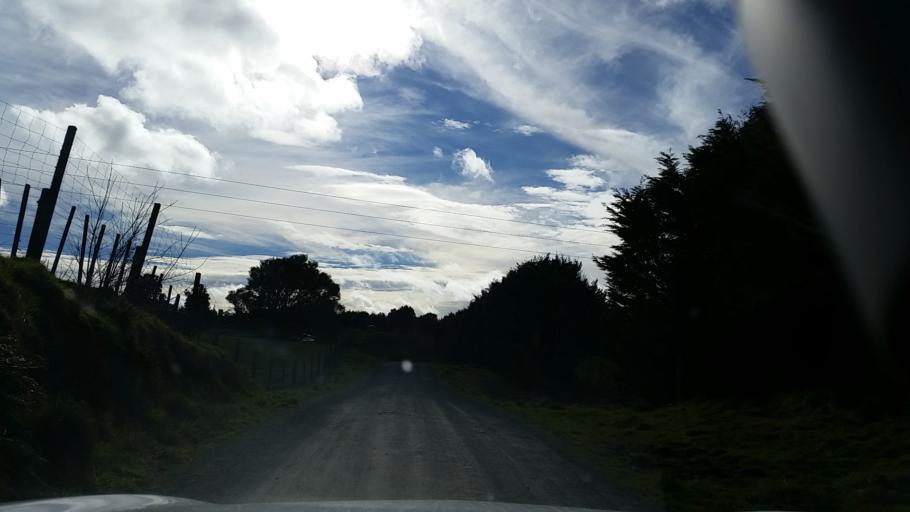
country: NZ
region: Bay of Plenty
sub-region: Rotorua District
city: Rotorua
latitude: -38.0955
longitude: 176.1038
